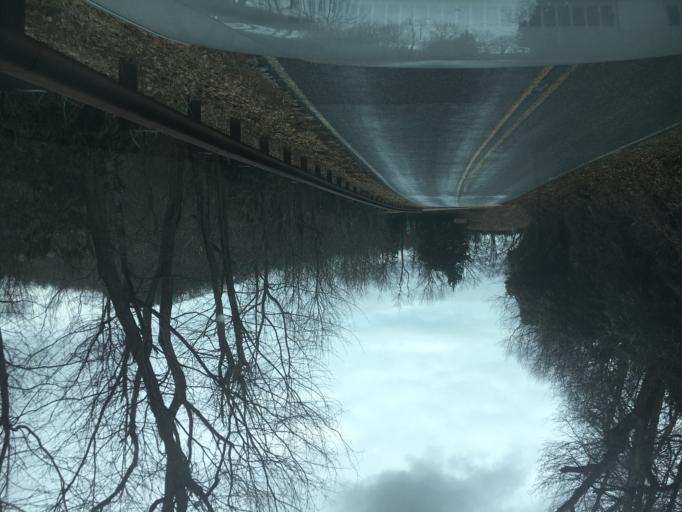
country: US
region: North Carolina
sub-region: Transylvania County
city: Brevard
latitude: 35.3723
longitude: -82.7900
